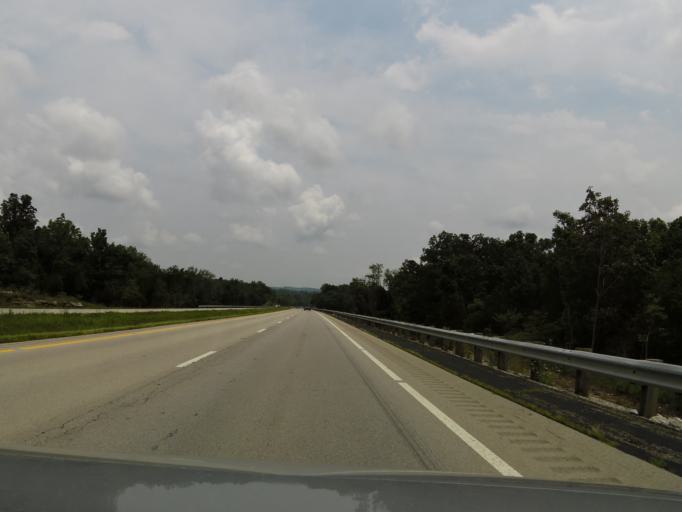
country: US
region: Kentucky
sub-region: Grayson County
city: Leitchfield
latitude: 37.5580
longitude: -86.0749
